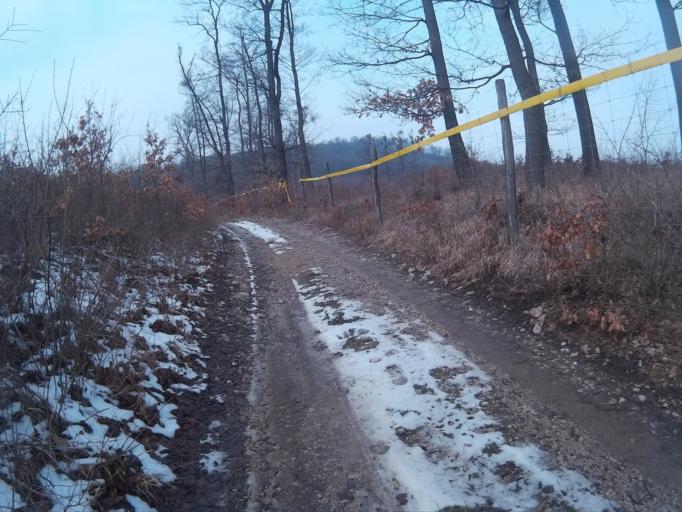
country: HU
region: Komarom-Esztergom
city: Labatlan
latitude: 47.6977
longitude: 18.5342
